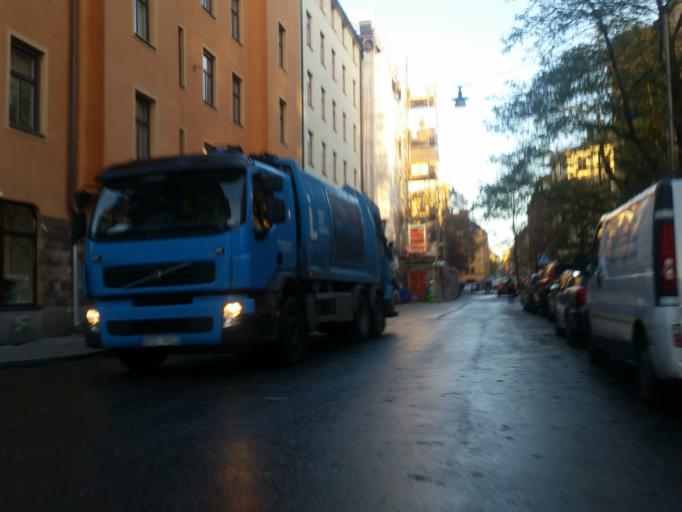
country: SE
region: Stockholm
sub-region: Stockholms Kommun
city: Stockholm
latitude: 59.3110
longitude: 18.0784
